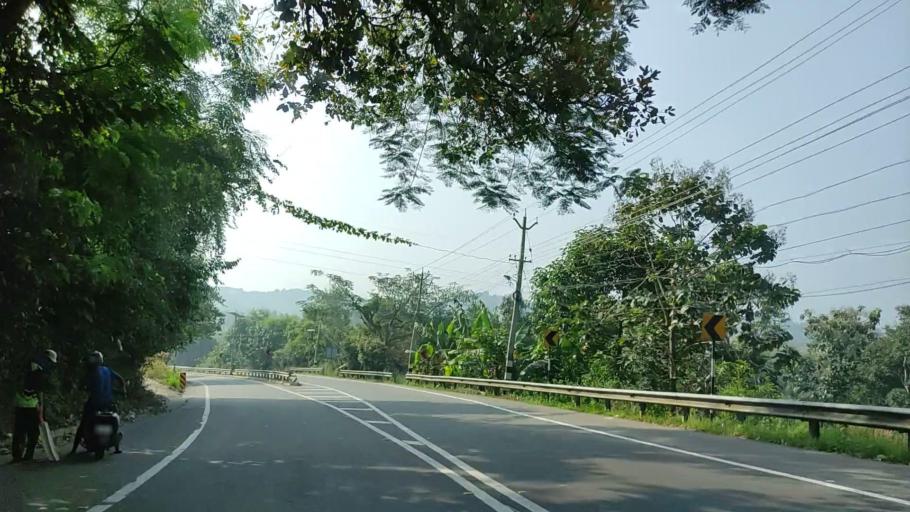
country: IN
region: Kerala
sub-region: Kollam
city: Punalur
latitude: 8.9774
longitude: 76.8144
